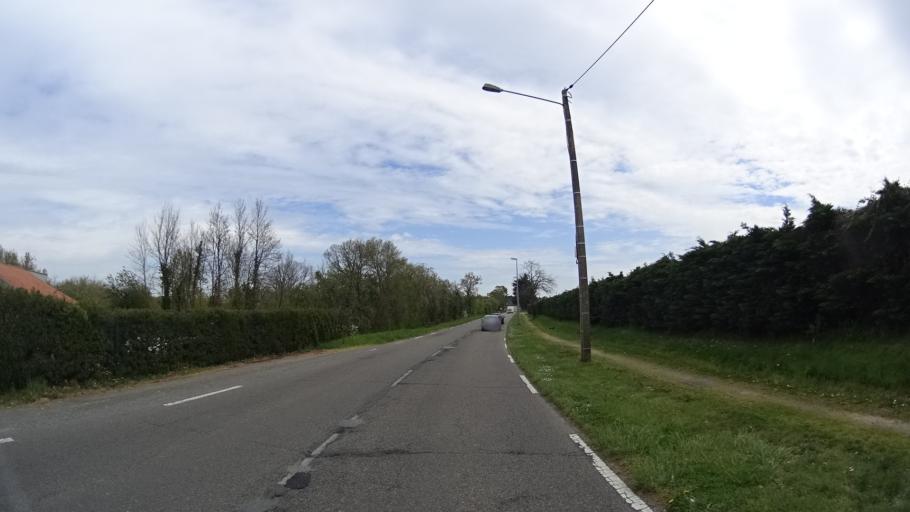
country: FR
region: Pays de la Loire
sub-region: Departement de la Loire-Atlantique
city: Bourgneuf-en-Retz
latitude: 47.0445
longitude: -1.9484
